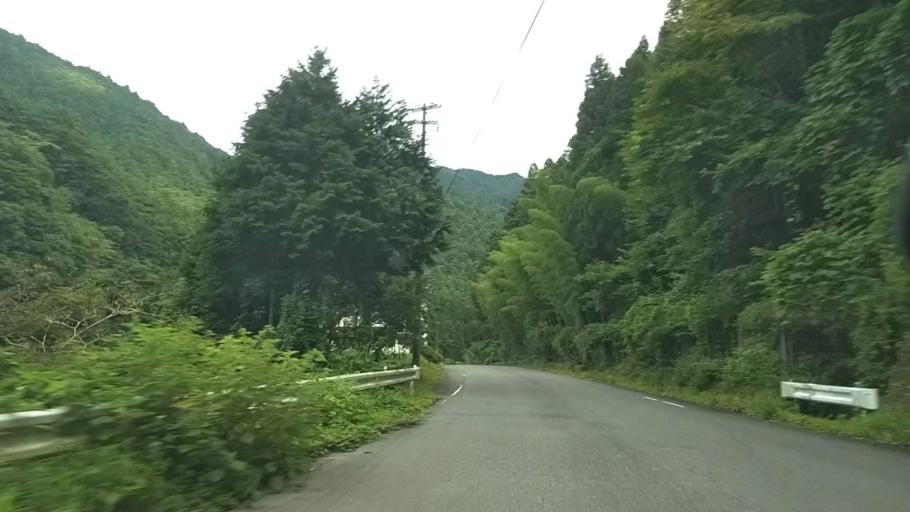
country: JP
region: Shizuoka
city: Fujinomiya
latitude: 35.1619
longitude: 138.5392
